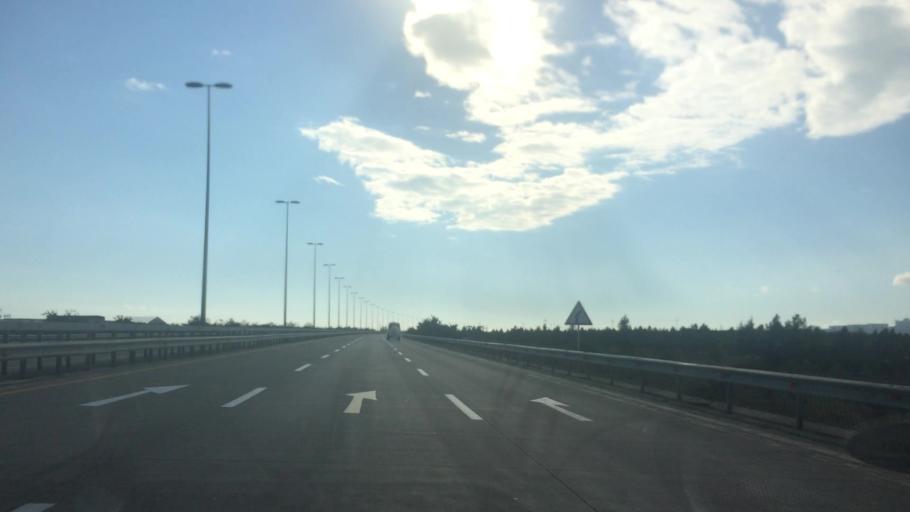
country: AZ
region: Baki
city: Hovsan
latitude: 40.3831
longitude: 50.0611
